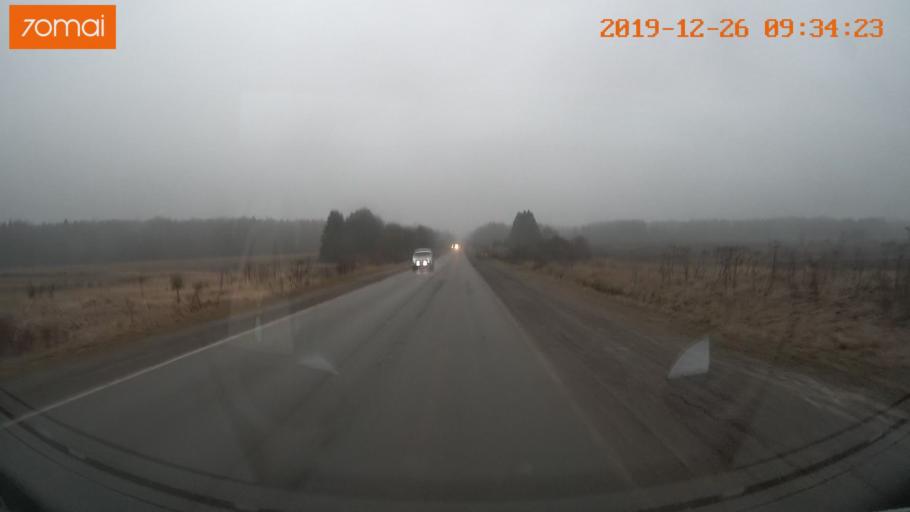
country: RU
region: Vologda
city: Vologda
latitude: 59.1009
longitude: 40.0871
